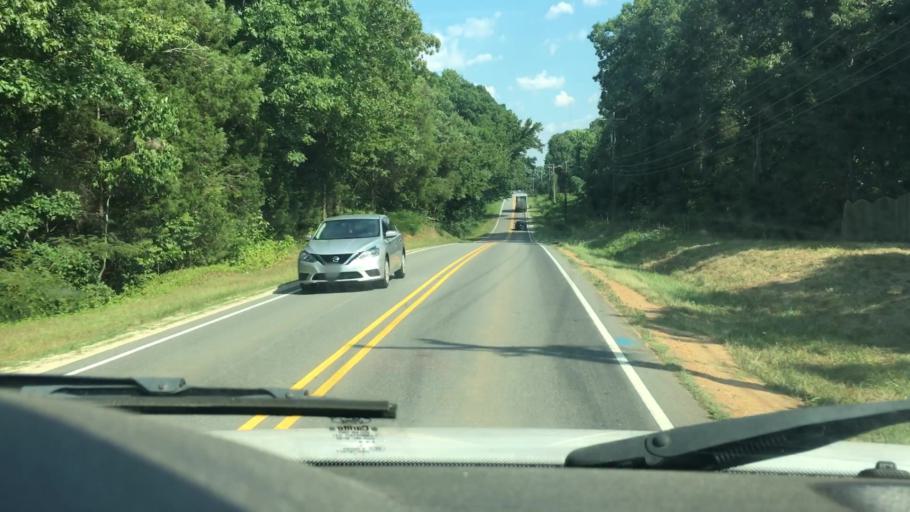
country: US
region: North Carolina
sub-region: Gaston County
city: Davidson
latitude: 35.4591
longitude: -80.8057
